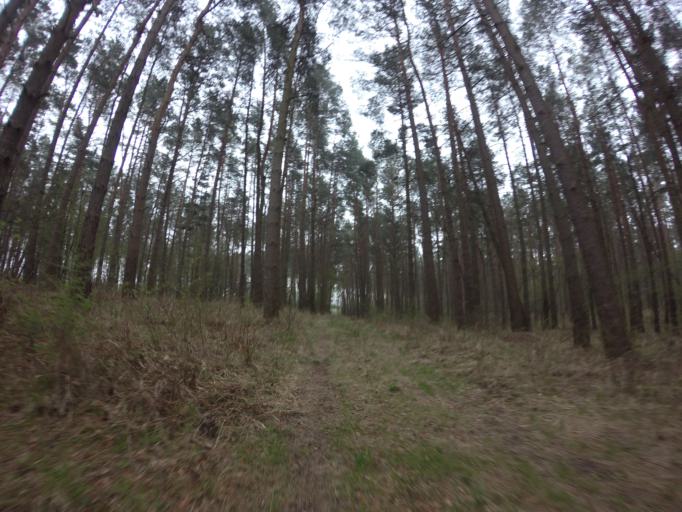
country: PL
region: West Pomeranian Voivodeship
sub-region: Powiat choszczenski
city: Recz
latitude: 53.1868
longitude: 15.5386
